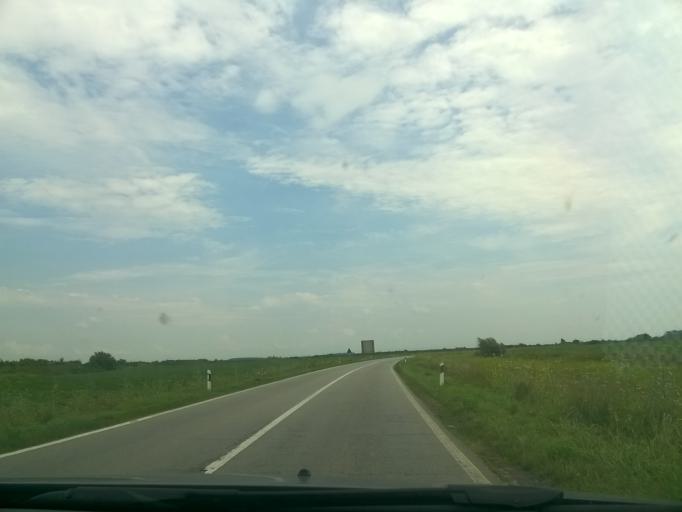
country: RS
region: Autonomna Pokrajina Vojvodina
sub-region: Juznobanatski Okrug
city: Plandiste
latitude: 45.2566
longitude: 21.0887
